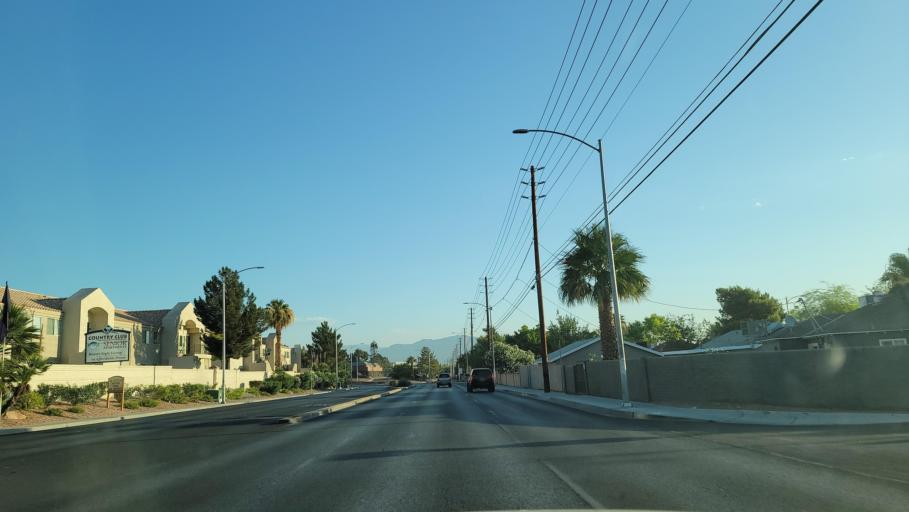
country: US
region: Nevada
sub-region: Clark County
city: Las Vegas
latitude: 36.1544
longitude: -115.1907
